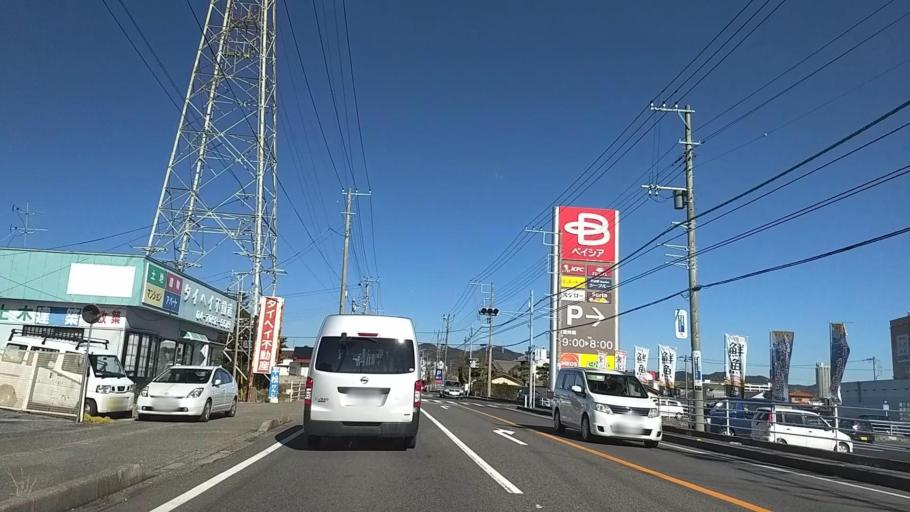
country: JP
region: Chiba
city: Kawaguchi
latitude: 35.1038
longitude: 140.0957
